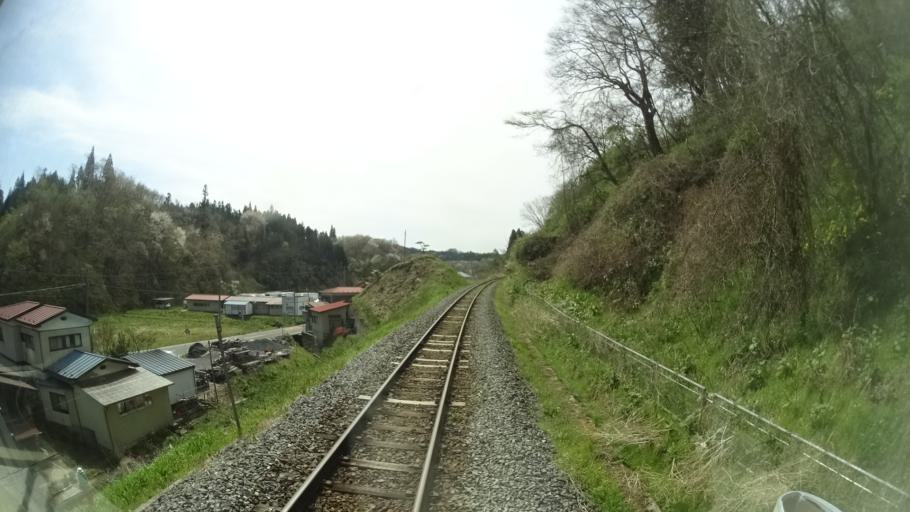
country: JP
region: Iwate
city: Ichinoseki
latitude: 38.9891
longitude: 141.3317
